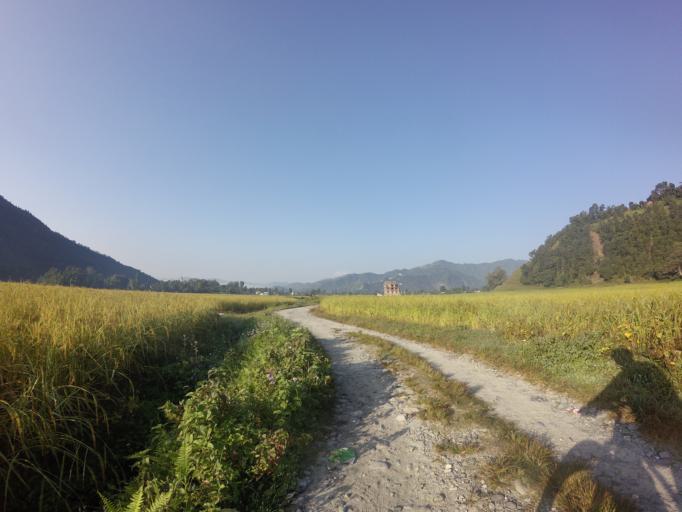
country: NP
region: Western Region
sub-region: Gandaki Zone
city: Pokhara
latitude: 28.2506
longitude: 84.0033
